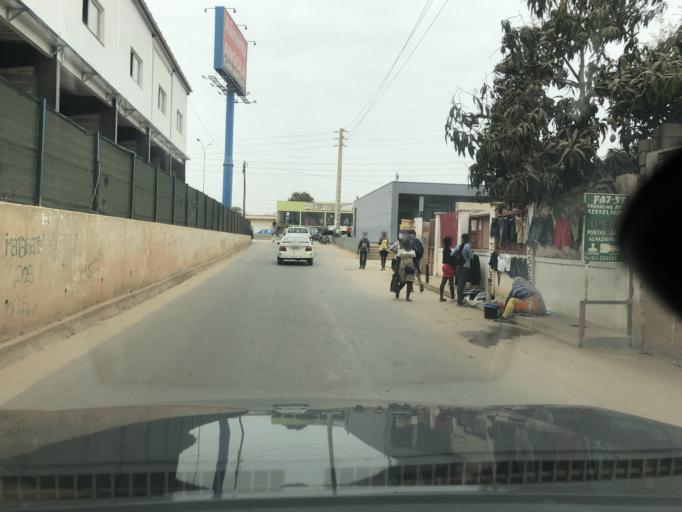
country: AO
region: Luanda
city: Luanda
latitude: -8.9010
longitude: 13.2587
